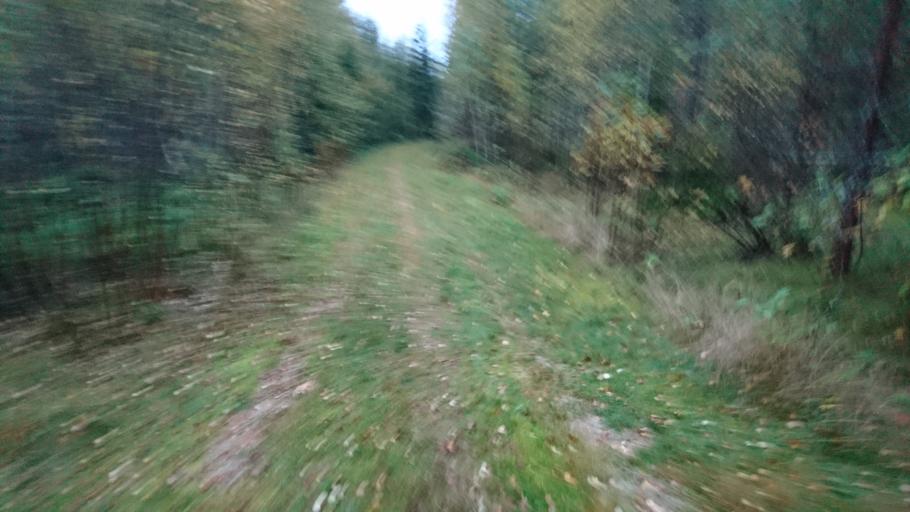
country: SE
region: Vaesterbotten
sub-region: Robertsfors Kommun
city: Robertsfors
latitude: 64.2311
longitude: 20.9945
